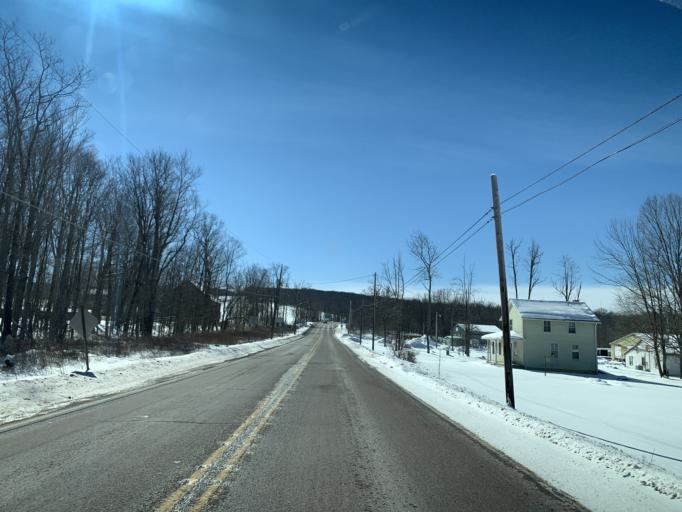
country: US
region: Pennsylvania
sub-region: Somerset County
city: Meyersdale
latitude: 39.7243
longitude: -79.0873
